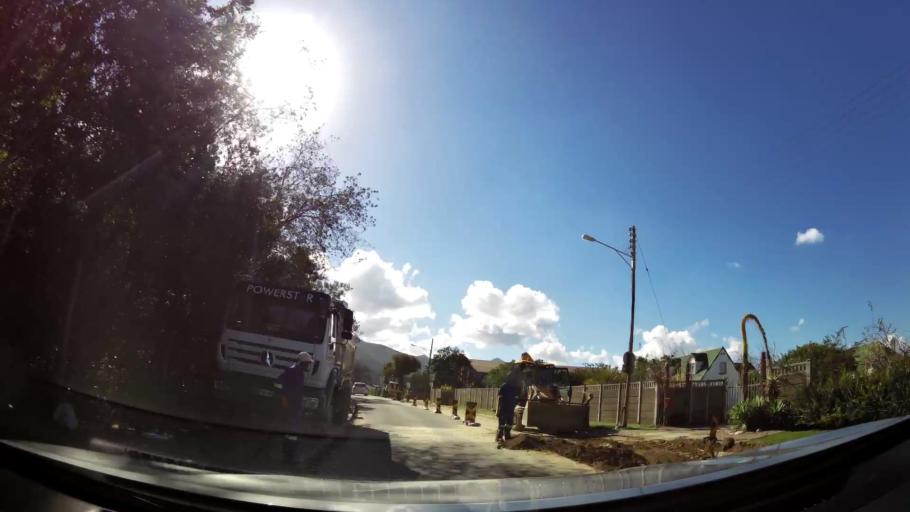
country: ZA
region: Western Cape
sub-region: Eden District Municipality
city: George
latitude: -33.9475
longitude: 22.4645
